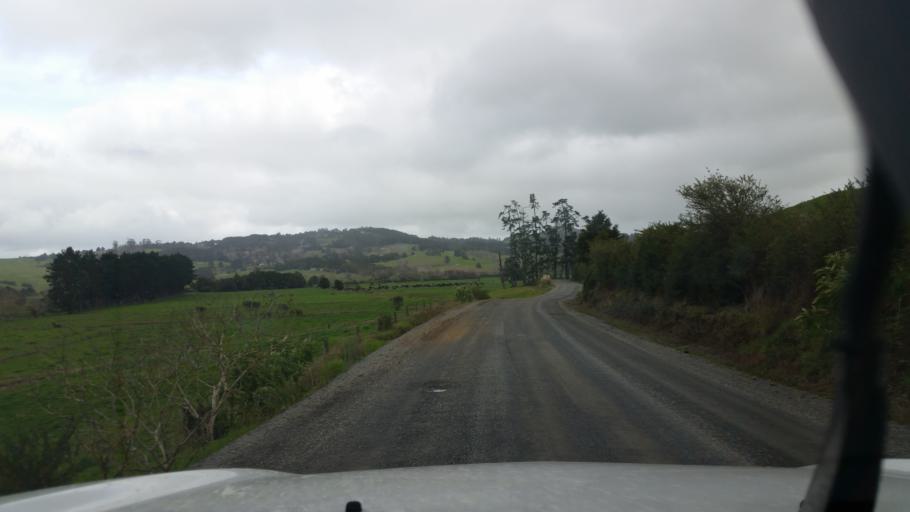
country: NZ
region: Northland
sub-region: Whangarei
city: Maungatapere
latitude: -35.6192
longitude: 174.1979
